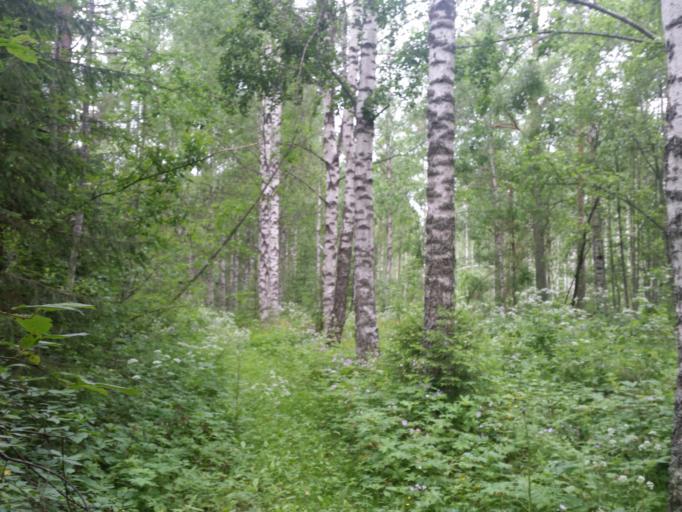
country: FI
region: Northern Savo
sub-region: Koillis-Savo
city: Kaavi
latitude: 62.9819
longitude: 28.7634
